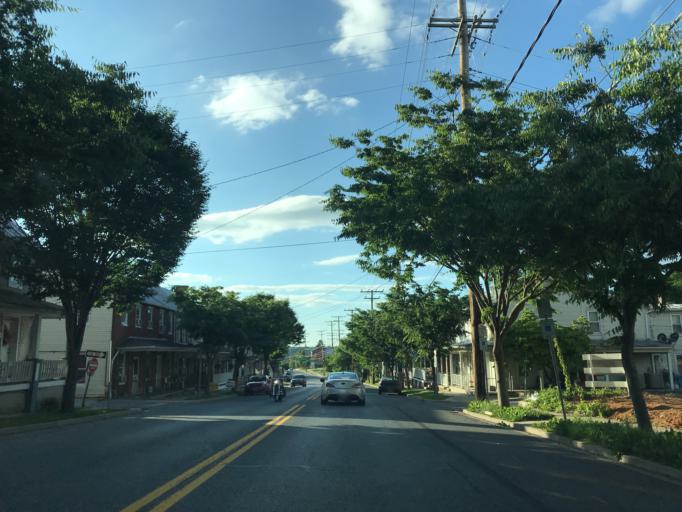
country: US
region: Maryland
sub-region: Carroll County
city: Manchester
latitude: 39.6629
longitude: -76.8856
